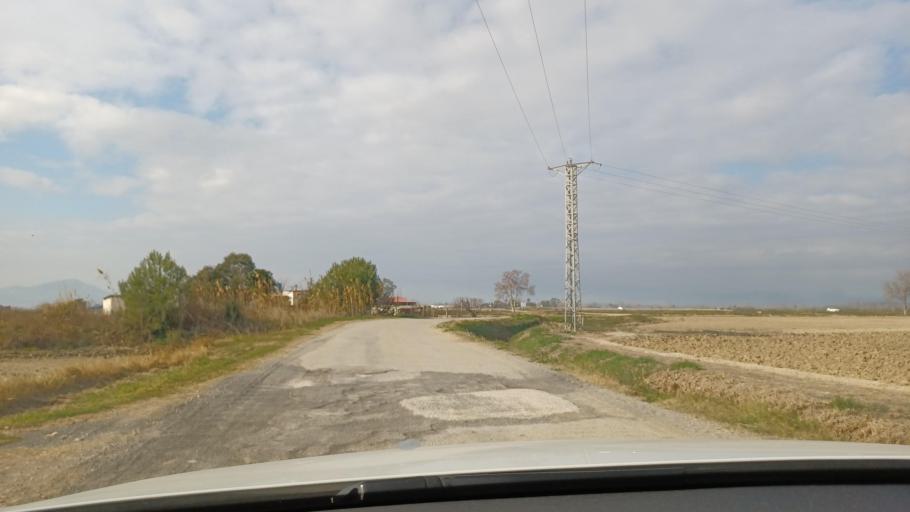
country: ES
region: Catalonia
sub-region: Provincia de Tarragona
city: Amposta
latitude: 40.7034
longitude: 0.6365
